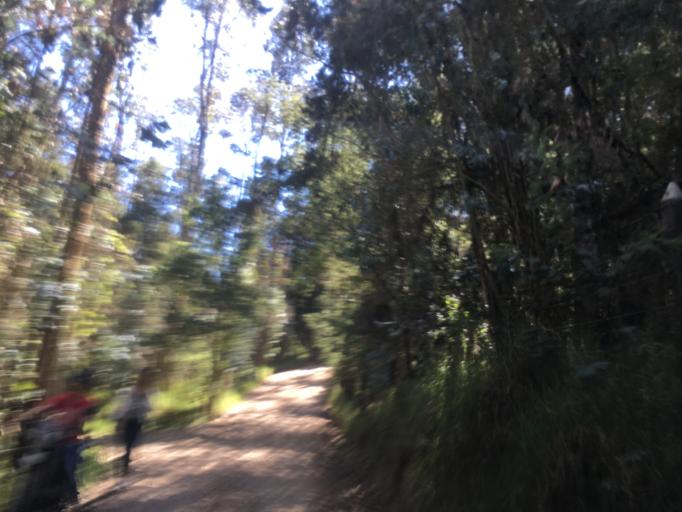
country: CO
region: Boyaca
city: Combita
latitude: 5.6668
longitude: -73.2799
